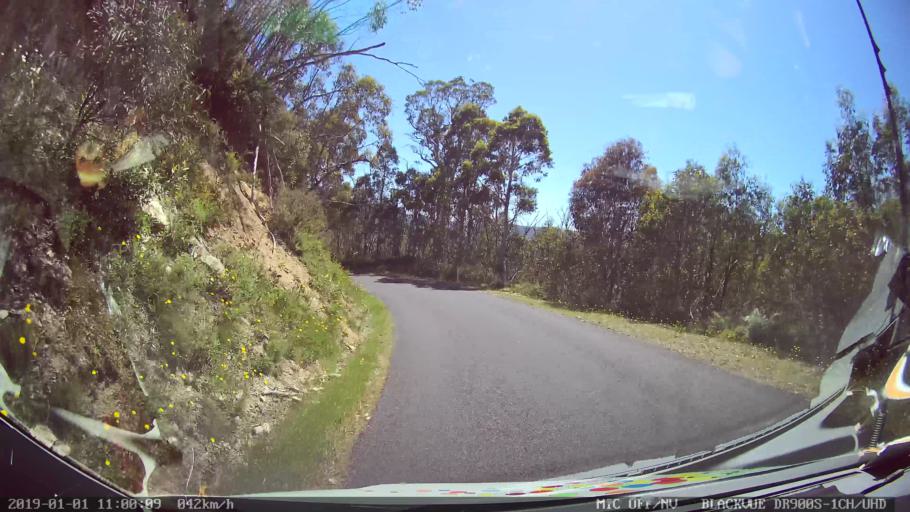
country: AU
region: New South Wales
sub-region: Snowy River
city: Jindabyne
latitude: -35.9823
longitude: 148.3969
